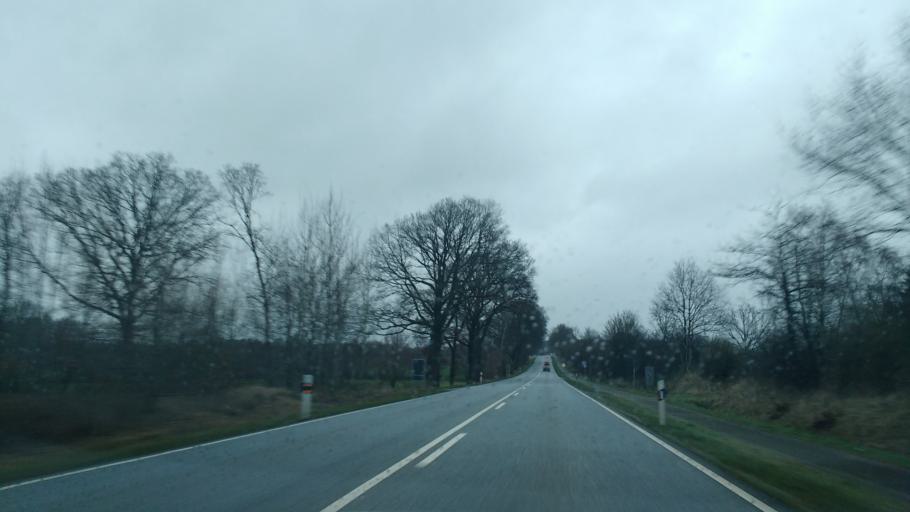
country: DE
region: Schleswig-Holstein
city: Silzen
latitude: 54.0484
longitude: 9.6230
